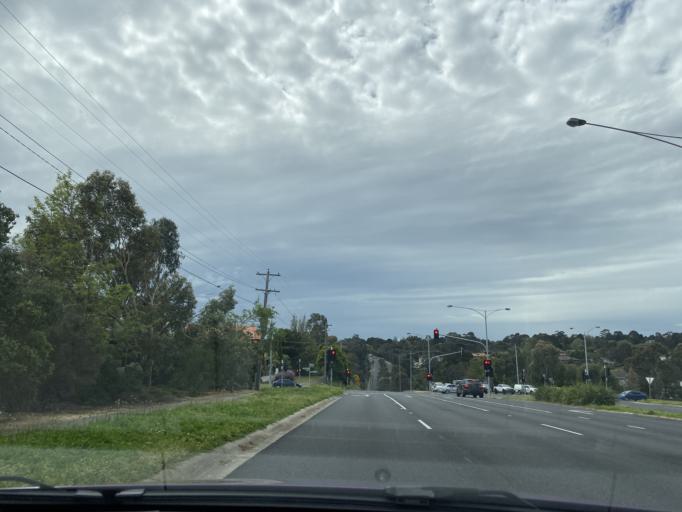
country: AU
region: Victoria
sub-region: Manningham
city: Templestowe Lower
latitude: -37.7706
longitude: 145.1290
